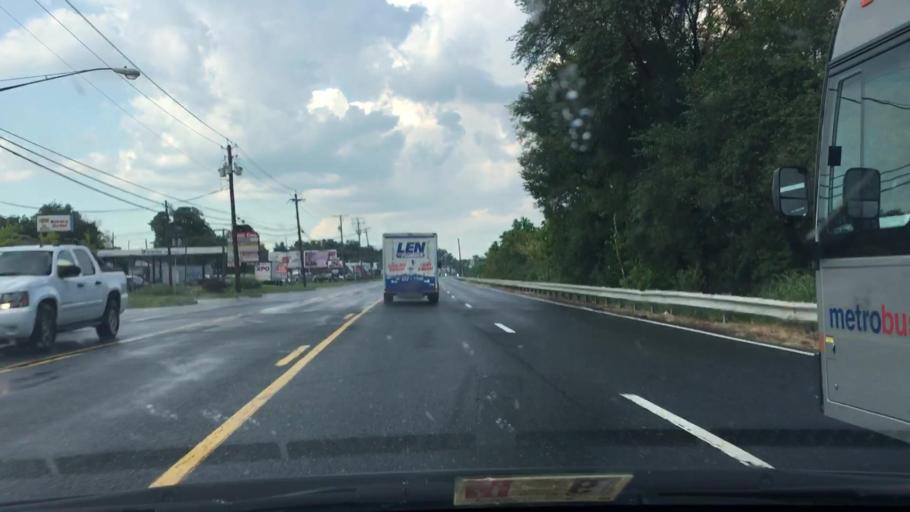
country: US
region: Maryland
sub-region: Prince George's County
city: Beltsville
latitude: 39.0401
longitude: -76.9047
